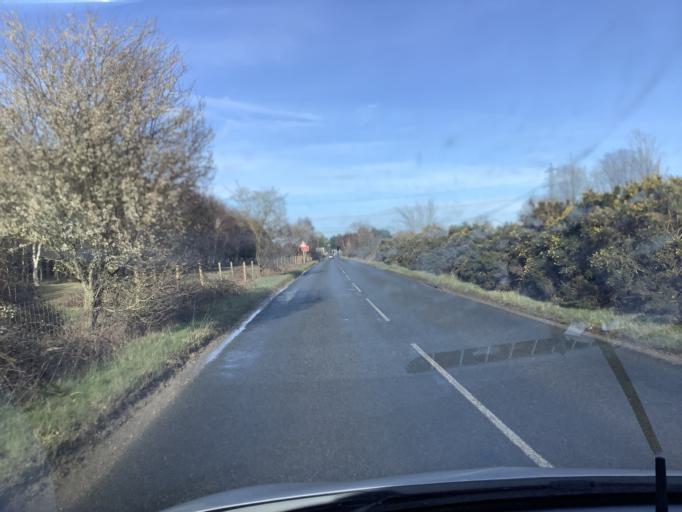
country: GB
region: England
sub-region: Hampshire
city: Hythe
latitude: 50.8481
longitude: -1.4226
